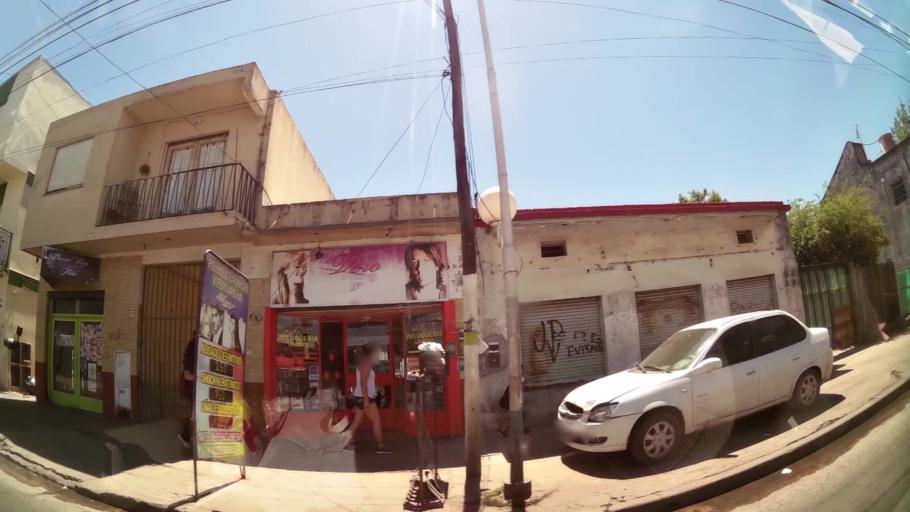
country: AR
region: Buenos Aires
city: Hurlingham
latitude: -34.5015
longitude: -58.6805
